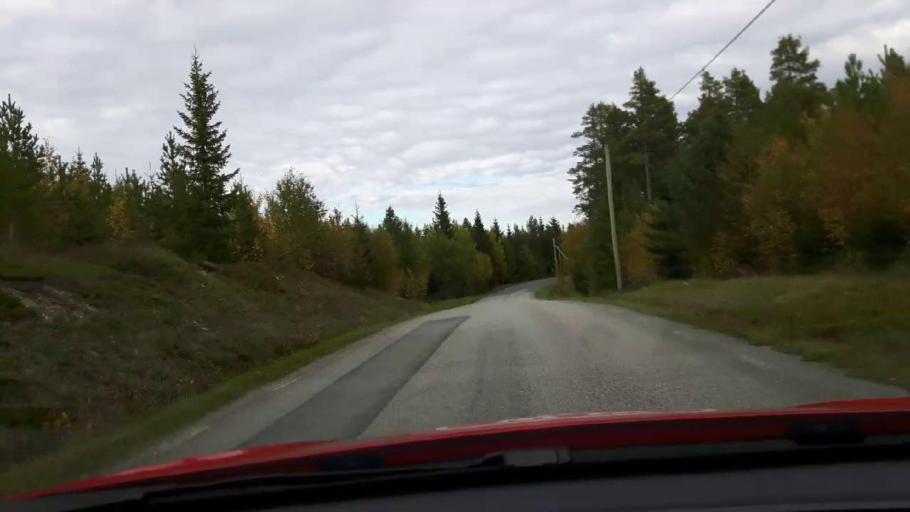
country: SE
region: Jaemtland
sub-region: Krokoms Kommun
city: Valla
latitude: 63.2593
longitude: 13.9900
